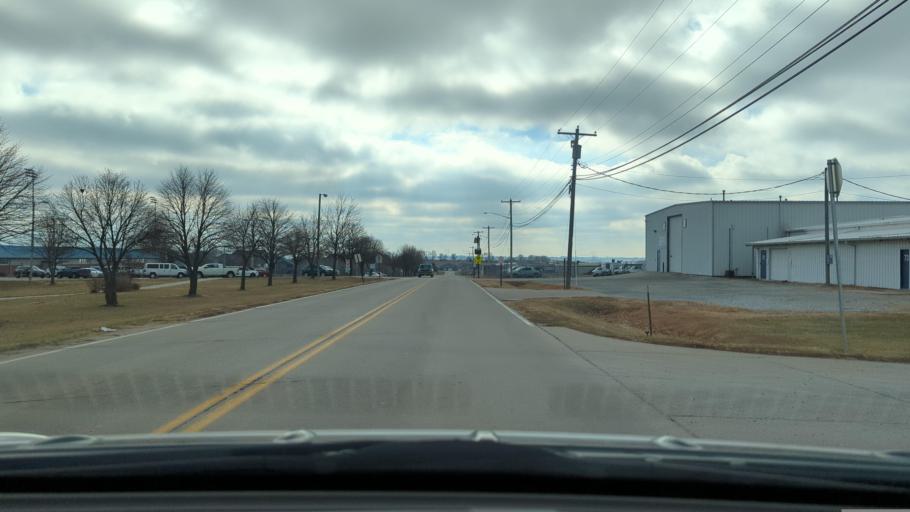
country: US
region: Nebraska
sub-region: Cass County
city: Plattsmouth
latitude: 41.0008
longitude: -95.9073
